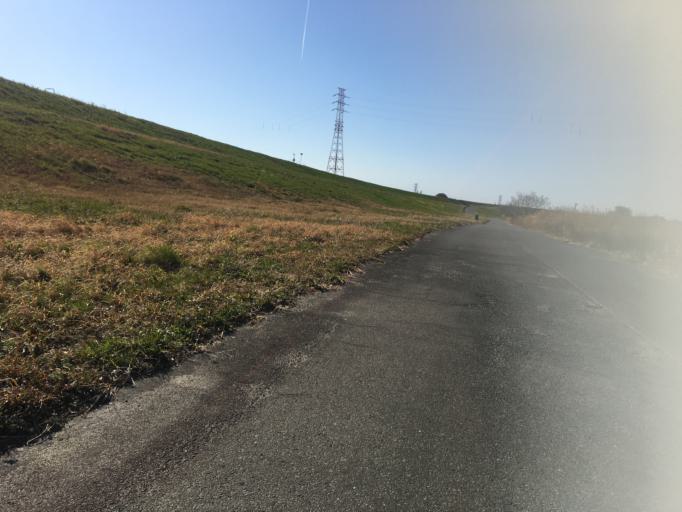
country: JP
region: Saitama
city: Shiki
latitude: 35.8309
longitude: 139.6097
